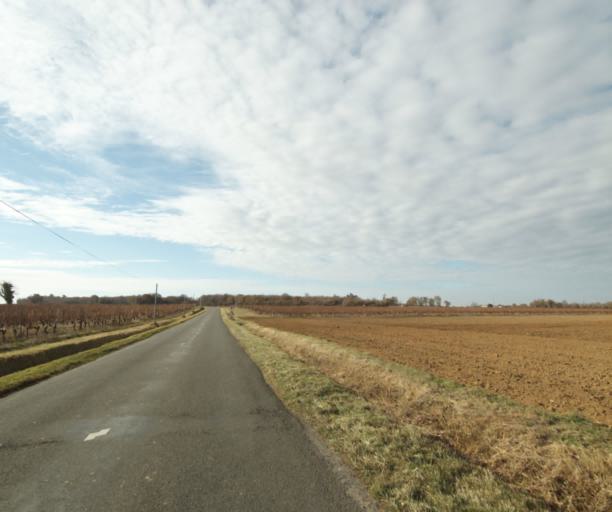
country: FR
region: Poitou-Charentes
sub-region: Departement de la Charente-Maritime
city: Corme-Royal
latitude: 45.7210
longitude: -0.8326
